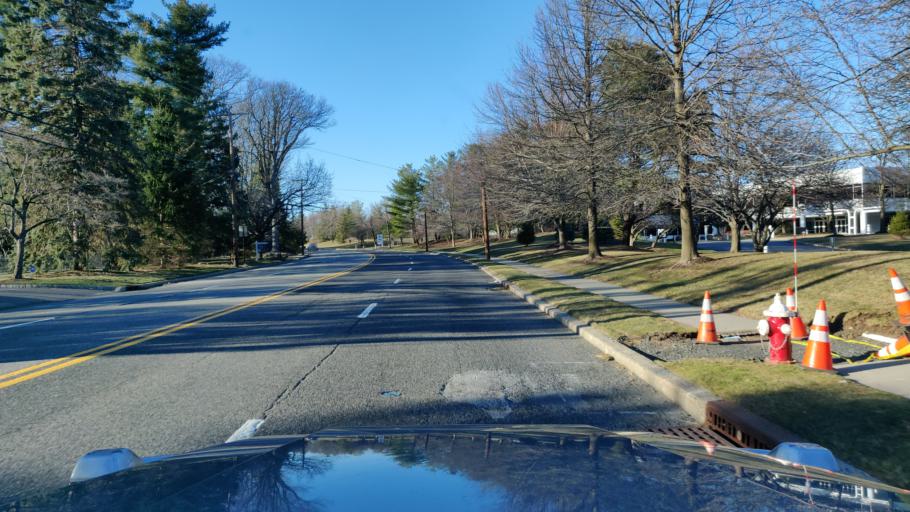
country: US
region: New Jersey
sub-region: Bergen County
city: Woodcliff Lake
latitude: 41.0337
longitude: -74.0739
